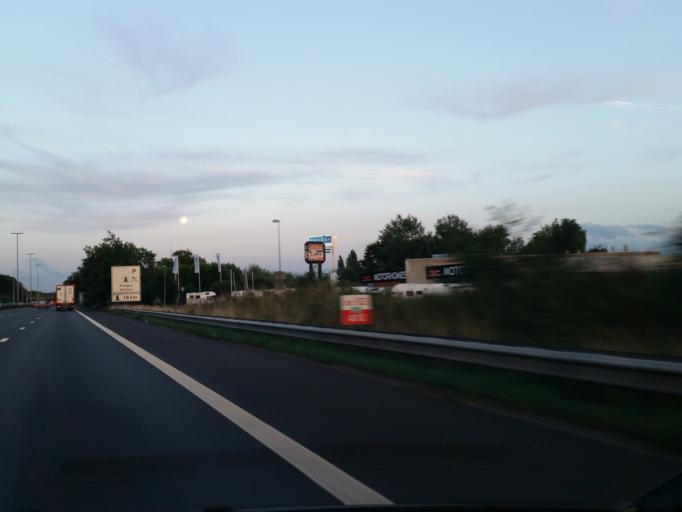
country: BE
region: Flanders
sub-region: Provincie Oost-Vlaanderen
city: Sint-Martens-Latem
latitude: 51.0430
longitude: 3.6038
